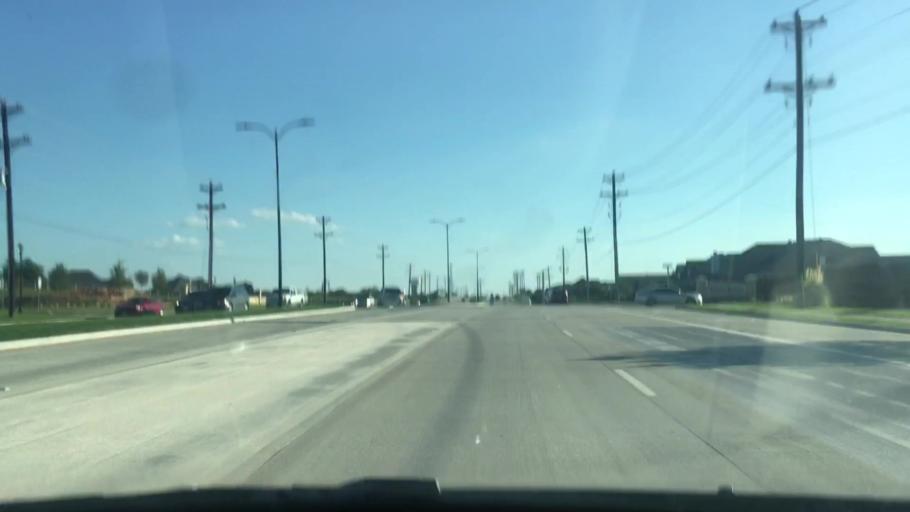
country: US
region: Texas
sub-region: Denton County
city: Little Elm
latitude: 33.2002
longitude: -96.8817
